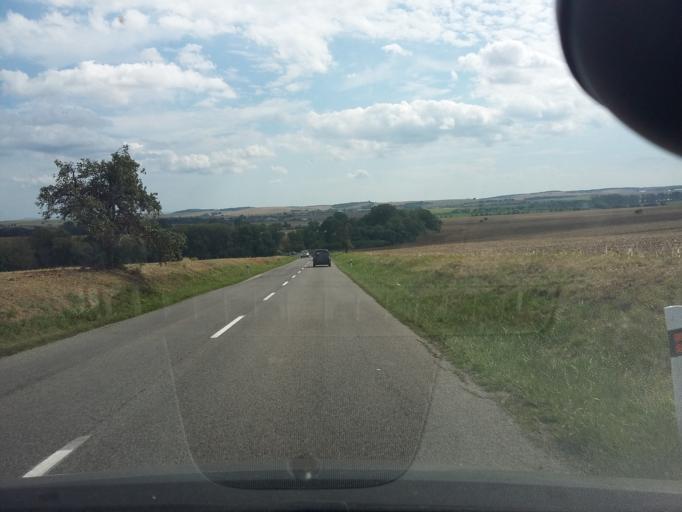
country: SK
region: Trnavsky
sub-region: Okres Skalica
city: Holic
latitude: 48.7535
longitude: 17.1707
